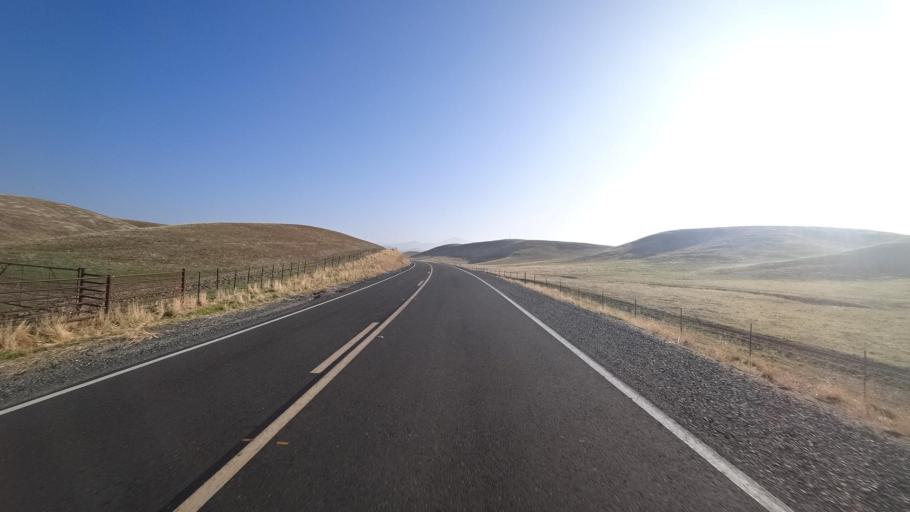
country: US
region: California
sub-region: Tulare County
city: Richgrove
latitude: 35.7442
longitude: -118.9392
